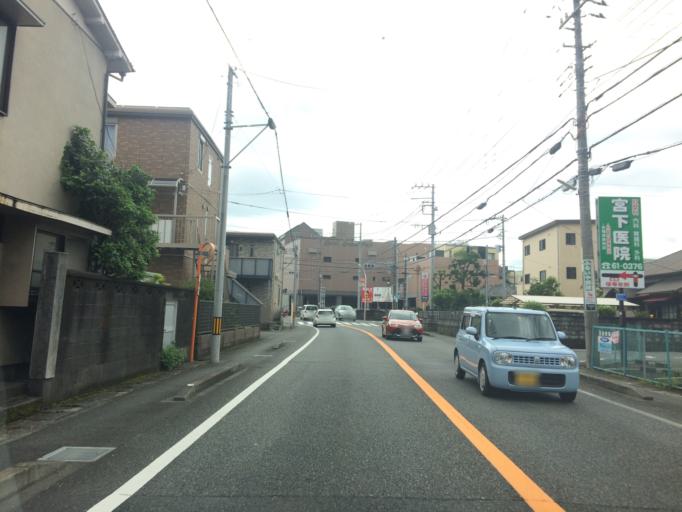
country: JP
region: Shizuoka
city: Fuji
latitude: 35.1563
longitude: 138.6491
